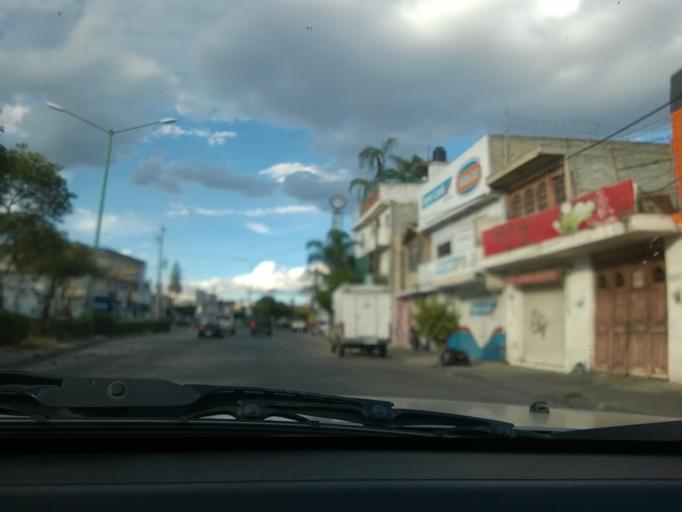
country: MX
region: Guanajuato
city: Leon
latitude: 21.1092
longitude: -101.6771
